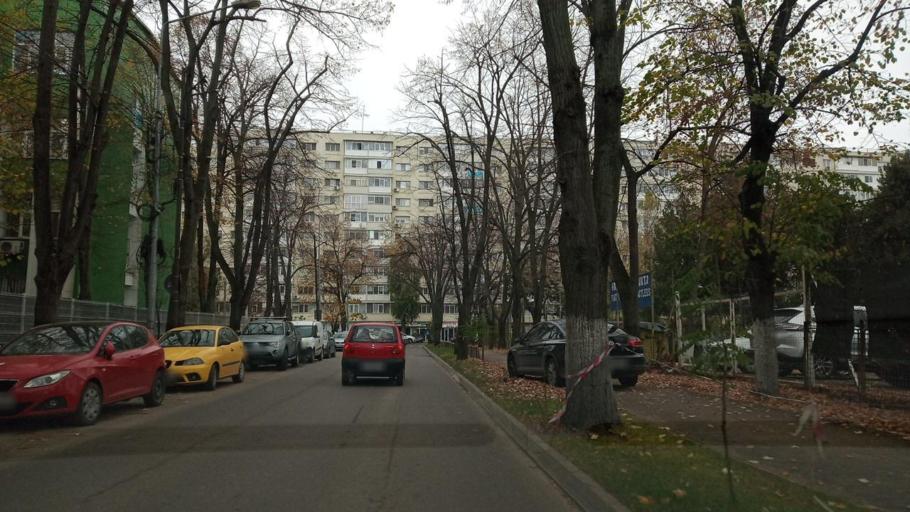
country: RO
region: Ilfov
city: Dobroesti
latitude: 44.4382
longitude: 26.1795
